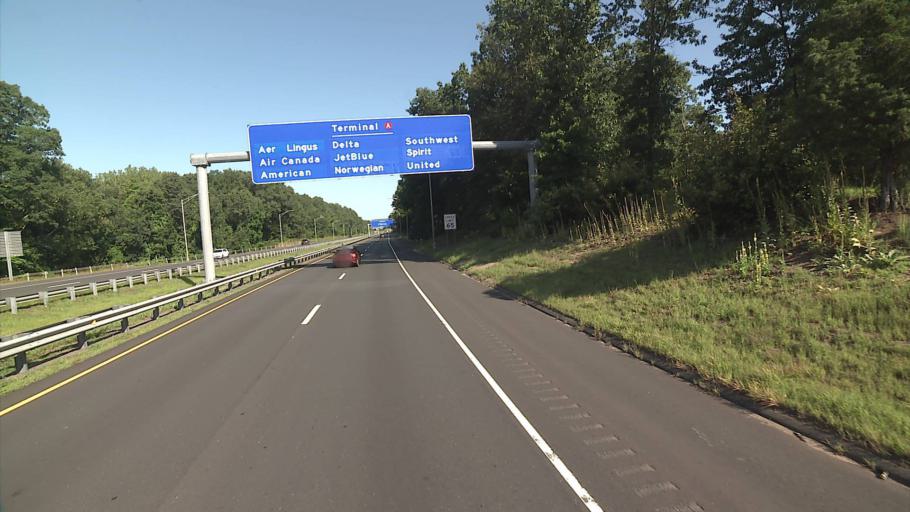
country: US
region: Connecticut
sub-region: Hartford County
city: Windsor Locks
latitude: 41.9094
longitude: -72.6647
